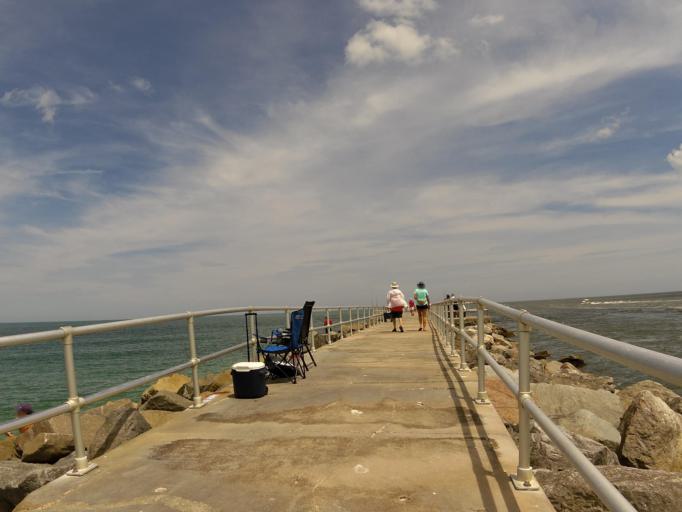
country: US
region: Florida
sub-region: Volusia County
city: Ponce Inlet
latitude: 29.0783
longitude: -80.9165
